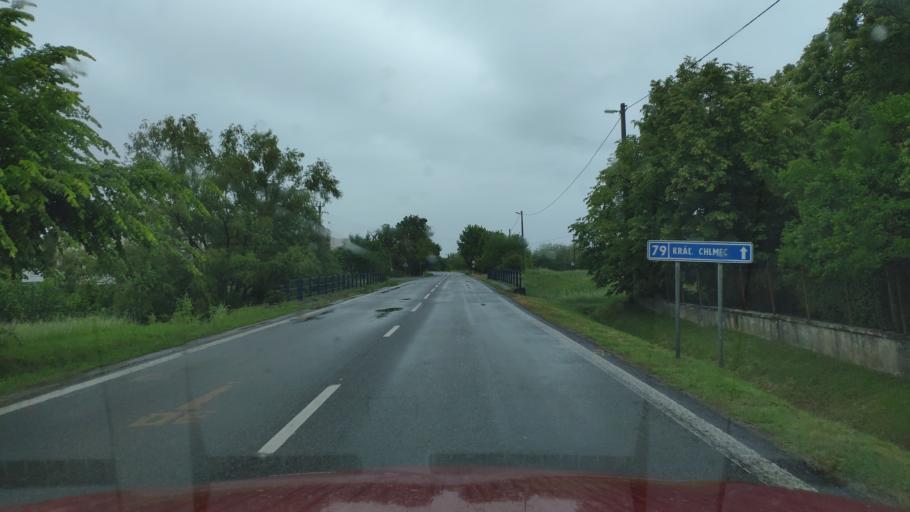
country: HU
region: Borsod-Abauj-Zemplen
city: Karcsa
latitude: 48.3966
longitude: 21.8062
